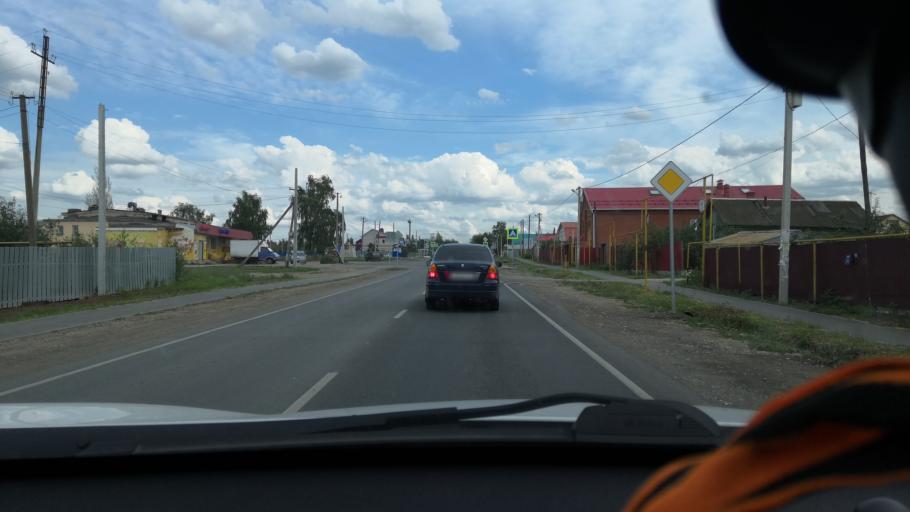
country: RU
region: Samara
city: Novosemeykino
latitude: 53.3768
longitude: 50.3457
